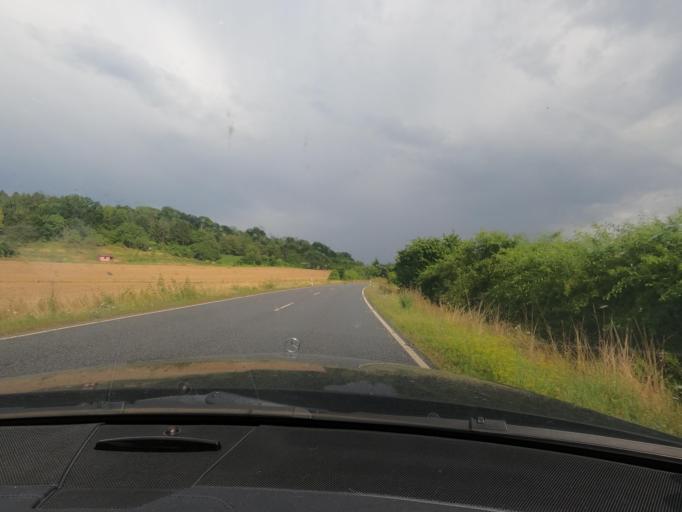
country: DE
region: Hesse
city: Wanfried
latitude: 51.1904
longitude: 10.1709
